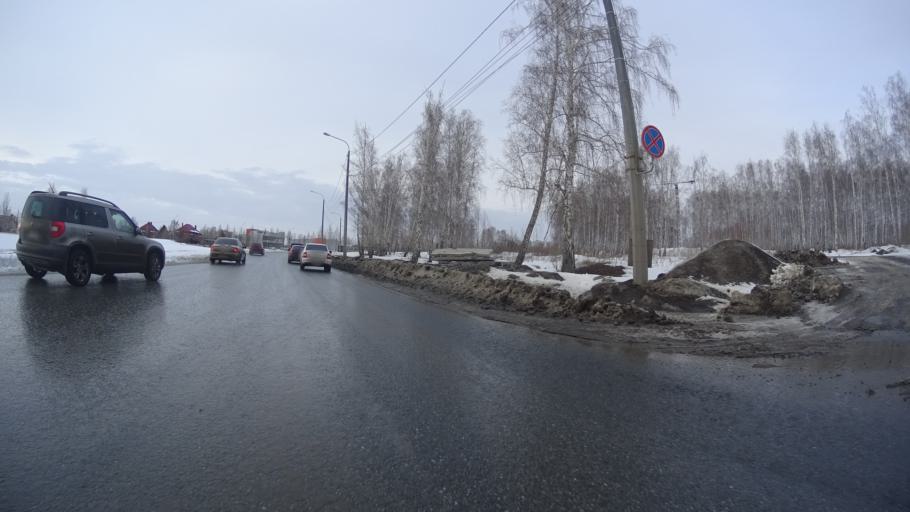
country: RU
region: Chelyabinsk
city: Roshchino
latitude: 55.1754
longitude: 61.2796
